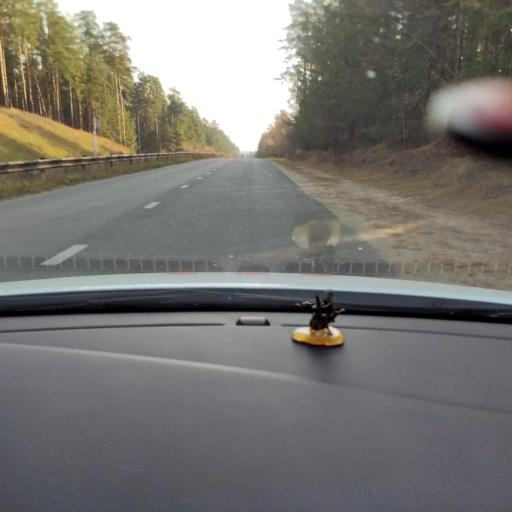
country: RU
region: Tatarstan
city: Osinovo
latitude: 55.8263
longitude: 48.8989
